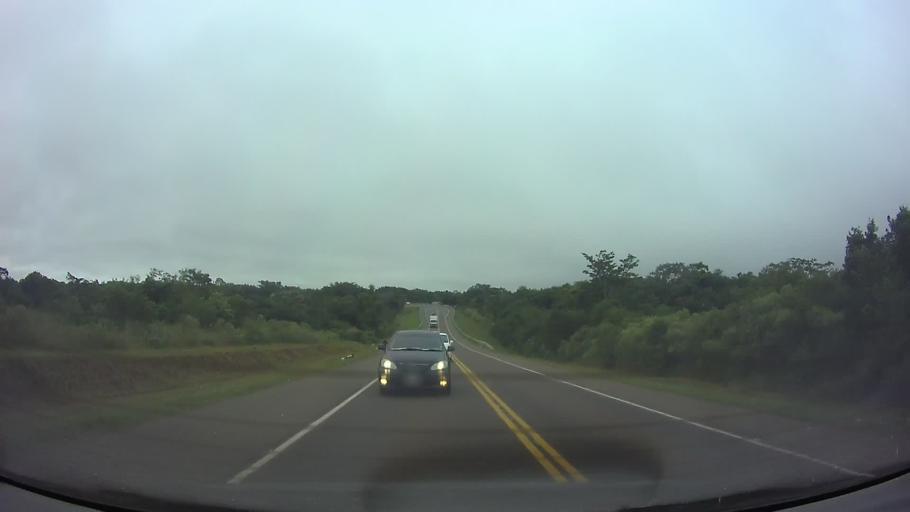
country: PY
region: Paraguari
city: Paraguari
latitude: -25.6068
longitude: -57.1857
